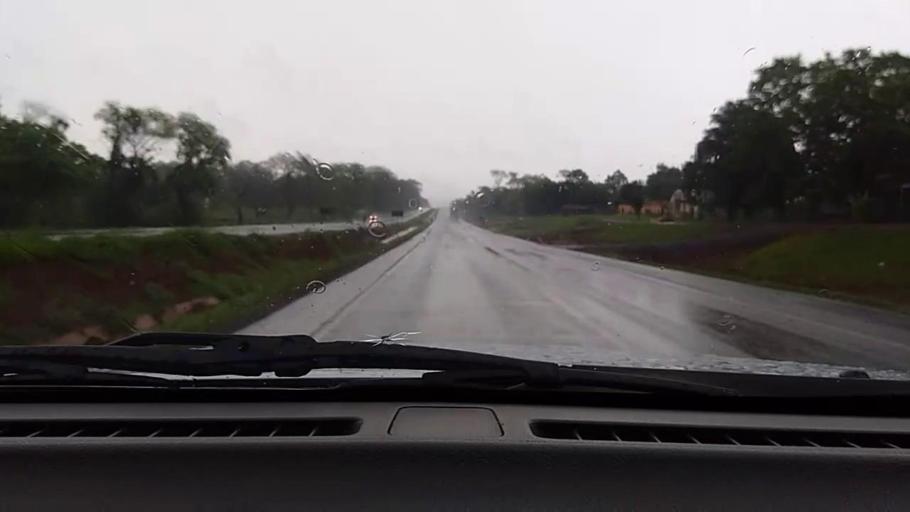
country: PY
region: Caaguazu
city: Repatriacion
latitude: -25.4484
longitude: -55.8947
